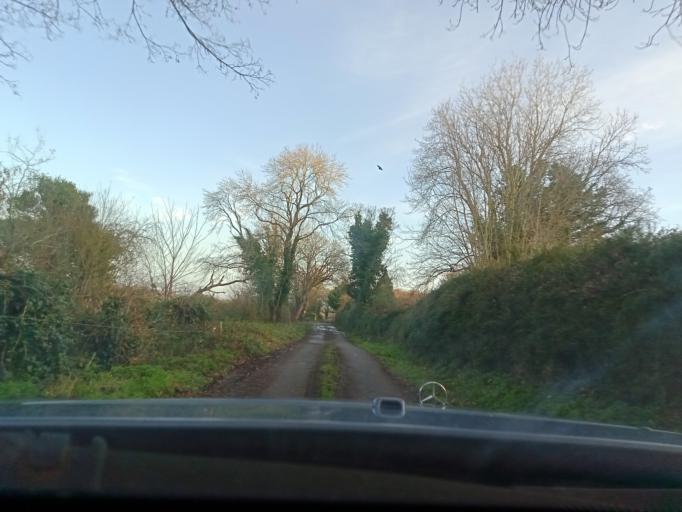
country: IE
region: Leinster
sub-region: Kilkenny
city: Callan
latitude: 52.4854
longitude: -7.4304
